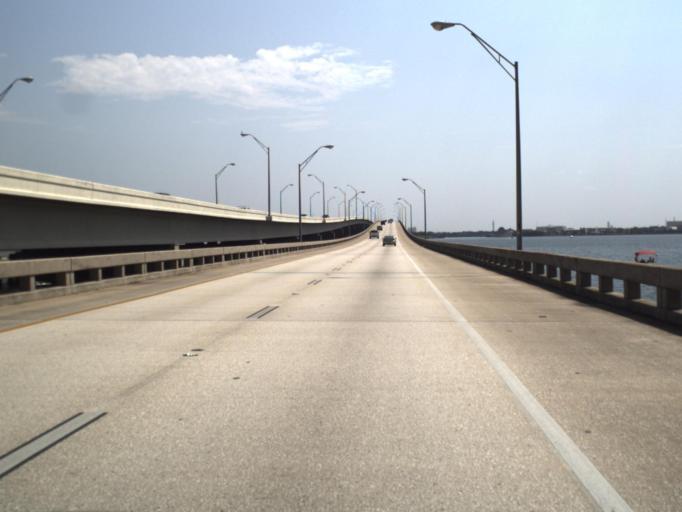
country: US
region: Florida
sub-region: Pinellas County
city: Gandy
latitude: 27.8858
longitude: -82.5586
